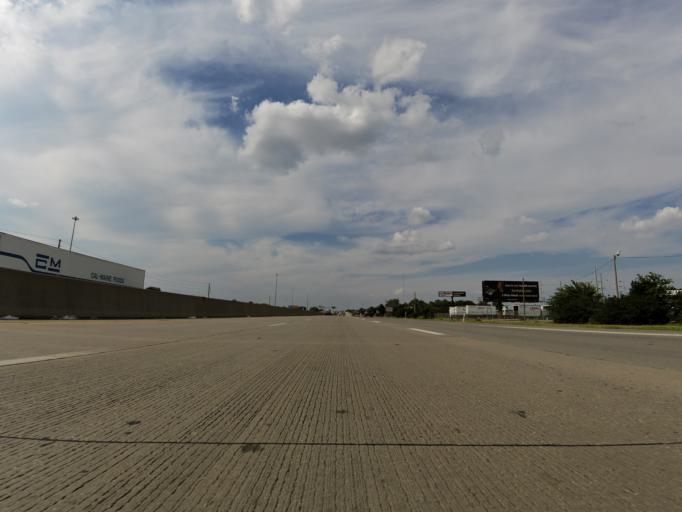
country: US
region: Kansas
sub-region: Sedgwick County
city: Park City
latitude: 37.7459
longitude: -97.3190
